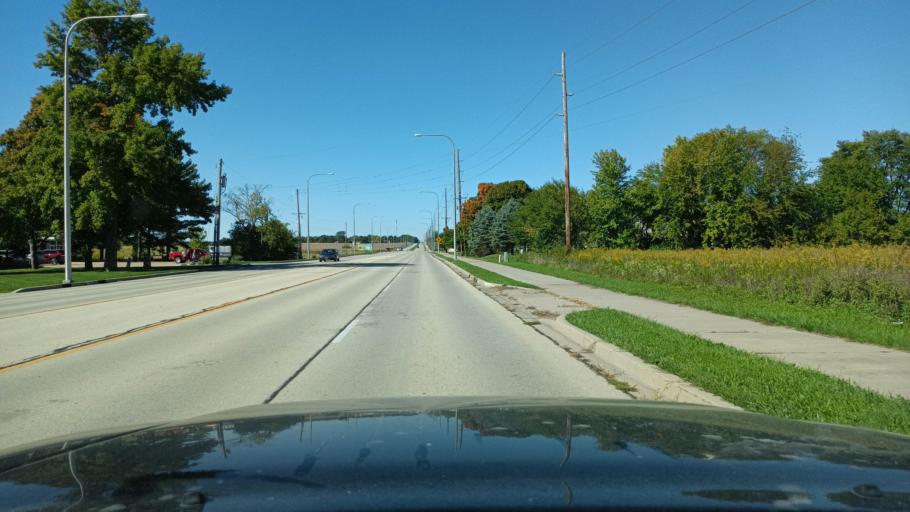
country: US
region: Illinois
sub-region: Champaign County
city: Urbana
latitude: 40.0841
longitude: -88.1658
